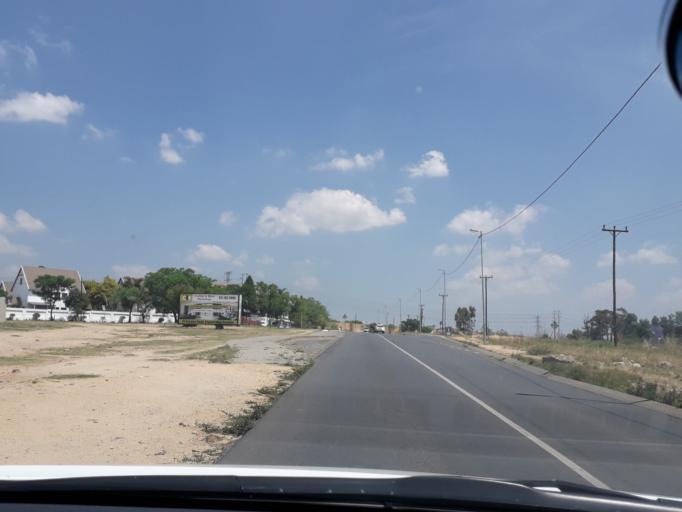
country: ZA
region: Gauteng
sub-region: City of Johannesburg Metropolitan Municipality
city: Midrand
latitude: -26.0118
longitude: 28.0770
